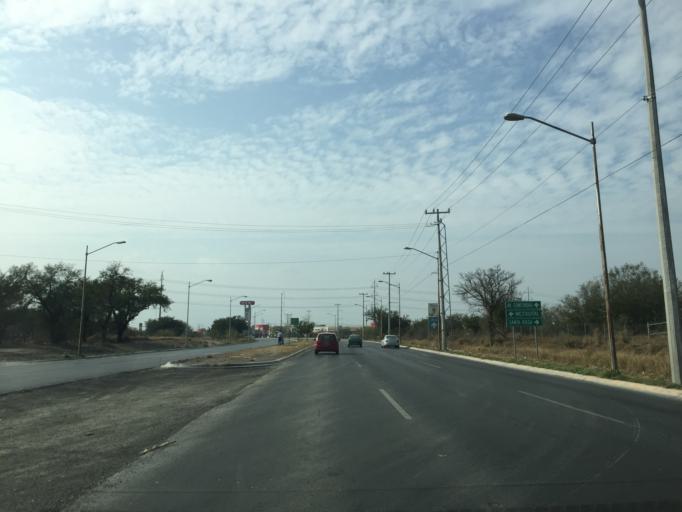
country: MX
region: Nuevo Leon
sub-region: Apodaca
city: Fraccionamiento Cosmopolis Octavo Sector
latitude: 25.7821
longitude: -100.2215
